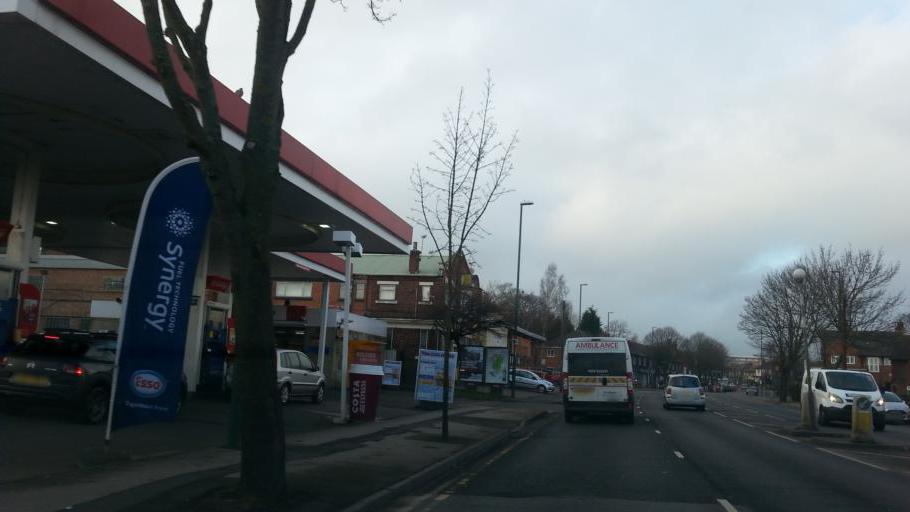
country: GB
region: England
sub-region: Nottingham
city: Nottingham
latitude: 52.9749
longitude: -1.1877
